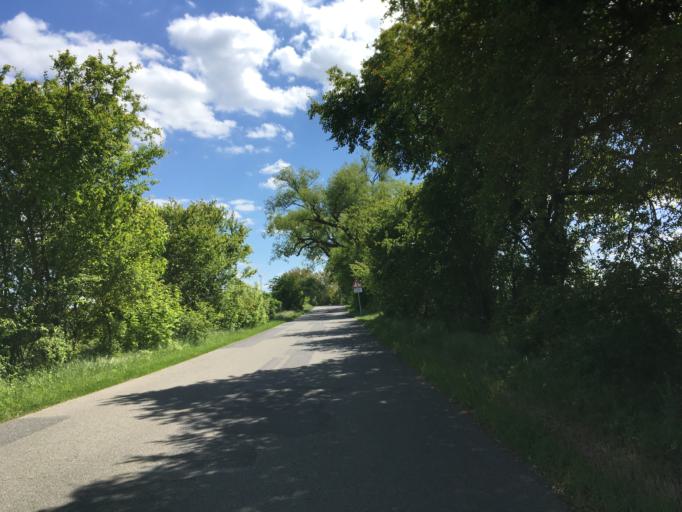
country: DE
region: Brandenburg
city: Rudnitz
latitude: 52.7056
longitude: 13.6619
